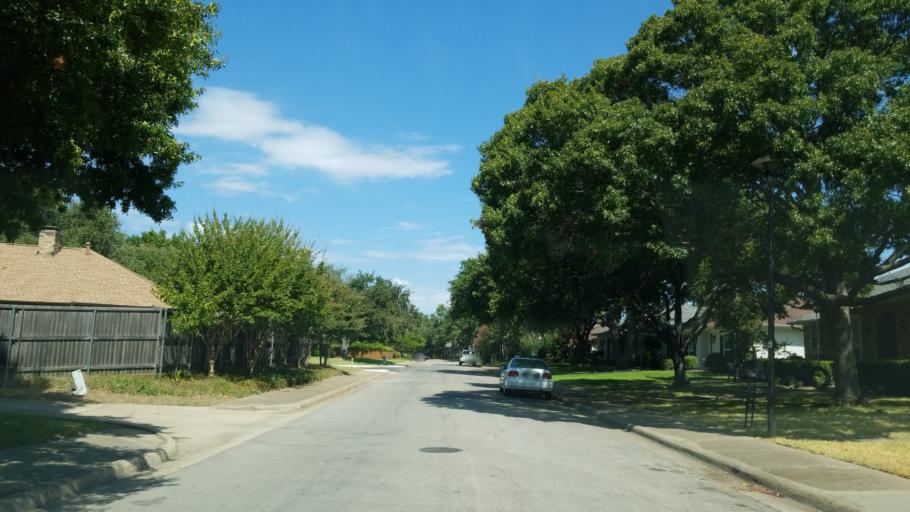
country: US
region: Texas
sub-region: Dallas County
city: Addison
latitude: 32.9696
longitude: -96.7858
